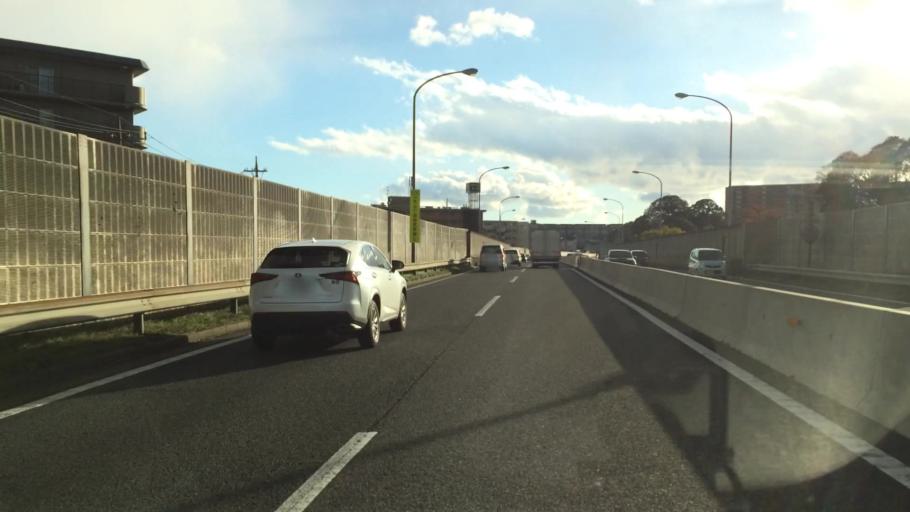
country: JP
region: Kanagawa
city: Fujisawa
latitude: 35.4195
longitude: 139.5380
